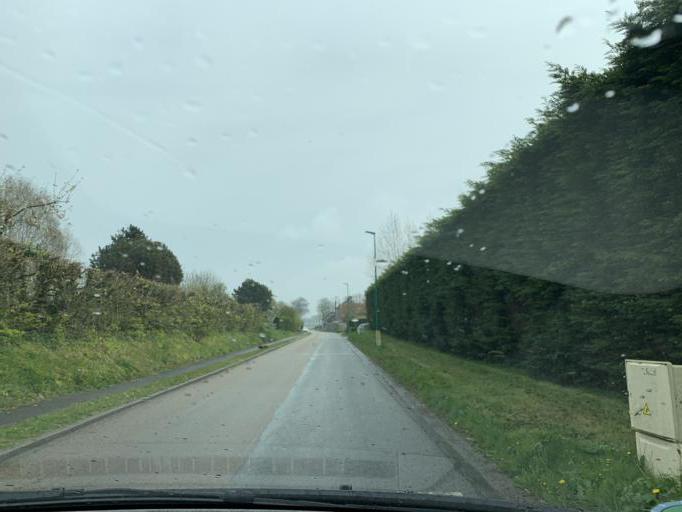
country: FR
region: Haute-Normandie
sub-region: Departement de la Seine-Maritime
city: Yport
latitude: 49.7374
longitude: 0.3372
